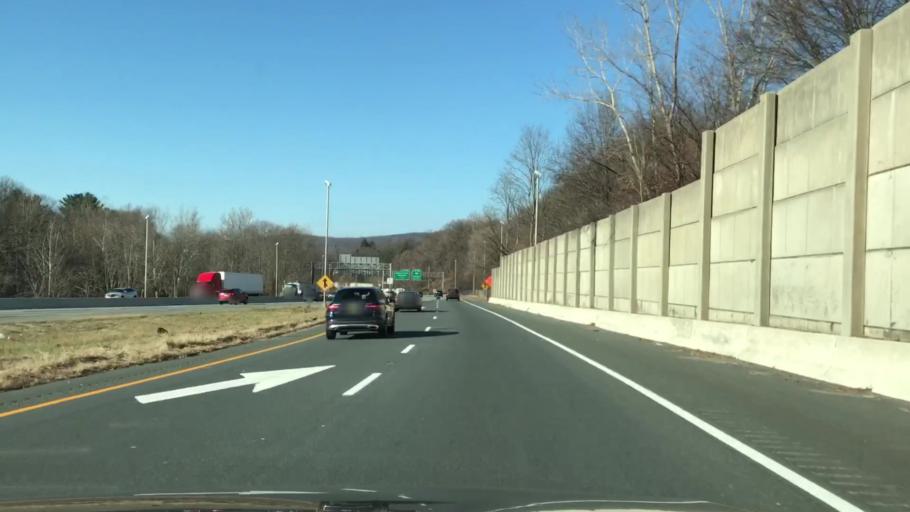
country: US
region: New Jersey
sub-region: Bergen County
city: Franklin Lakes
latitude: 41.0239
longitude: -74.2252
